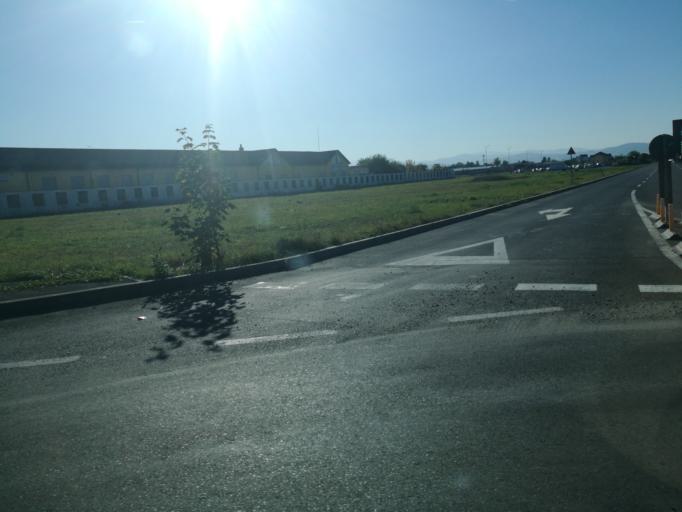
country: RO
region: Brasov
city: Brasov
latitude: 45.6731
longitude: 25.5896
